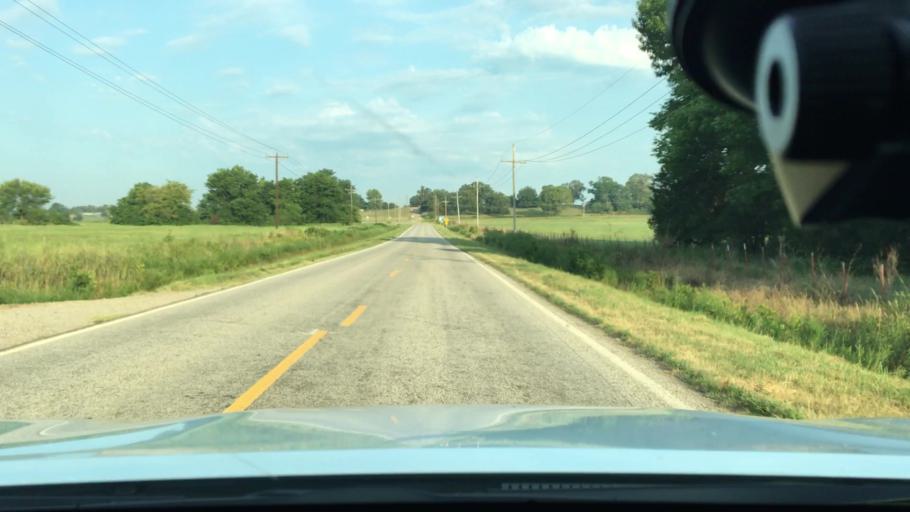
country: US
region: Arkansas
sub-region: Johnson County
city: Coal Hill
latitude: 35.3376
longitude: -93.6262
